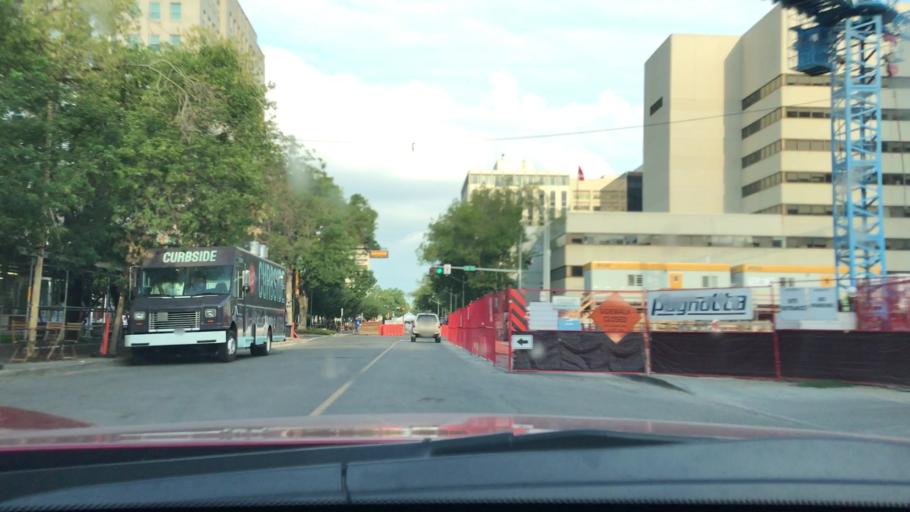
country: CA
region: Alberta
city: Edmonton
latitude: 53.5373
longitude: -113.5037
